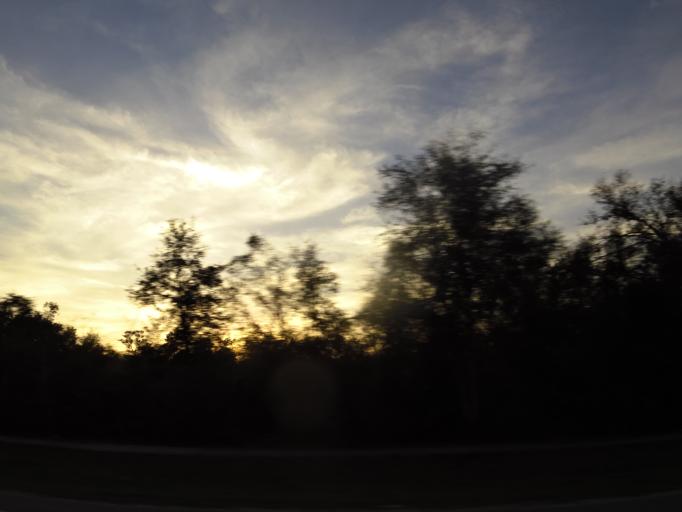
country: US
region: Florida
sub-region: Volusia County
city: North DeLand
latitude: 29.0757
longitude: -81.3049
